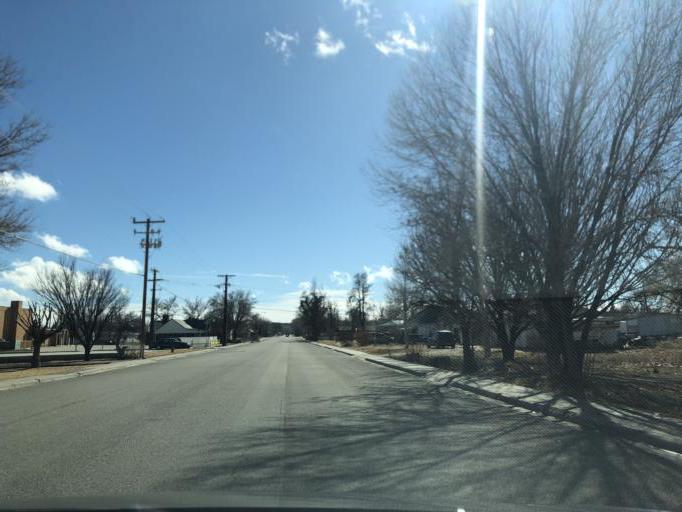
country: US
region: Utah
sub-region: Carbon County
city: East Carbon City
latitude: 38.9979
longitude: -110.1622
